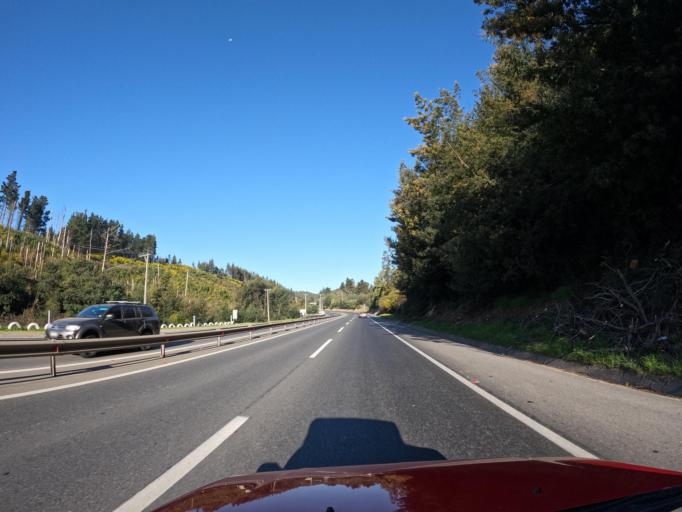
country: CL
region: Biobio
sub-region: Provincia de Concepcion
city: Penco
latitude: -36.7517
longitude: -72.9867
